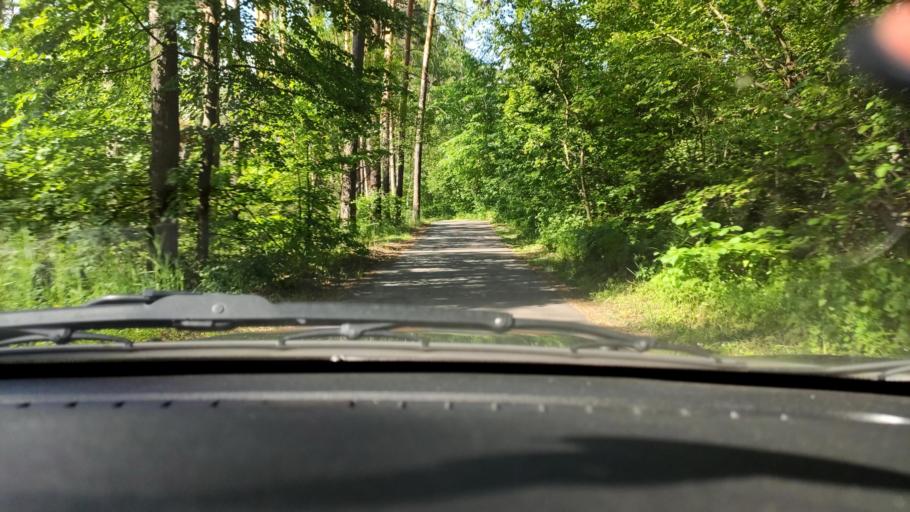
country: RU
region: Voronezj
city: Somovo
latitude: 51.8010
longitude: 39.3804
